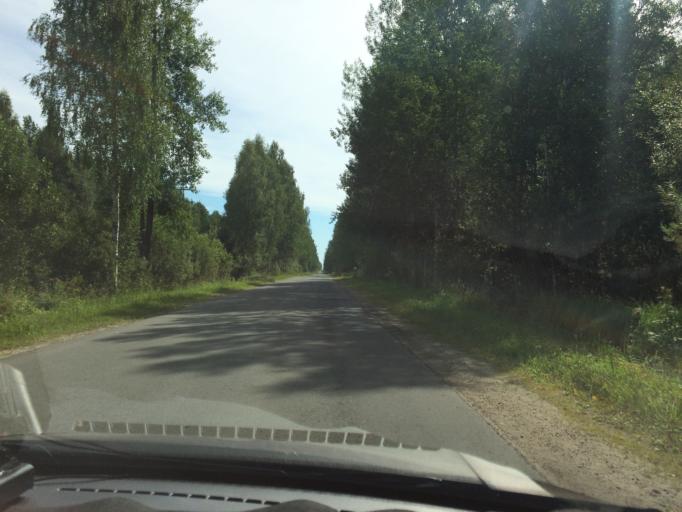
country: RU
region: Mariy-El
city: Surok
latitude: 56.5700
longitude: 48.2327
